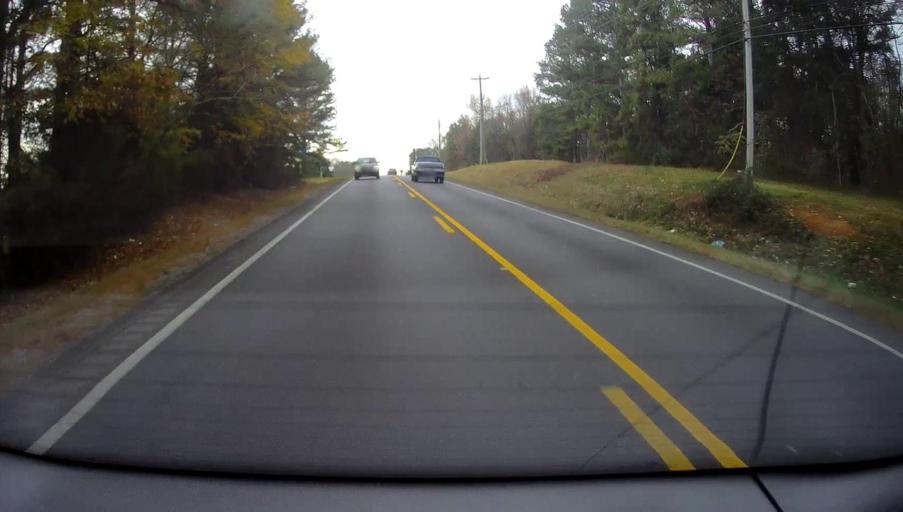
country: US
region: Alabama
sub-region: Morgan County
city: Priceville
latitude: 34.5040
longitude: -86.8633
